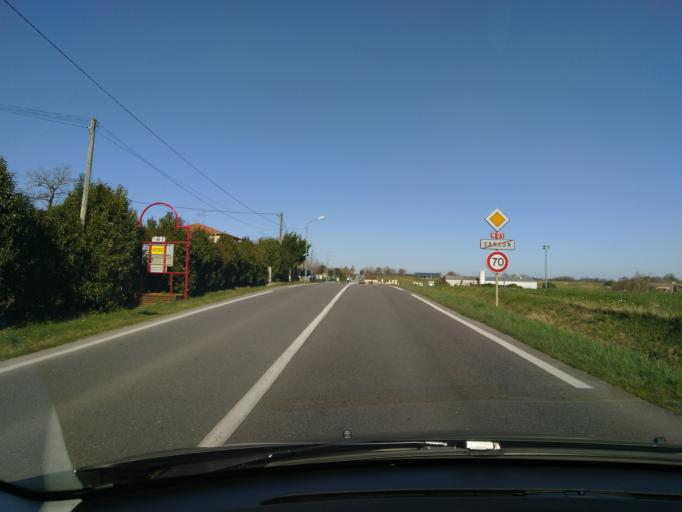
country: FR
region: Aquitaine
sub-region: Departement du Lot-et-Garonne
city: Cancon
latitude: 44.5443
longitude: 0.6253
